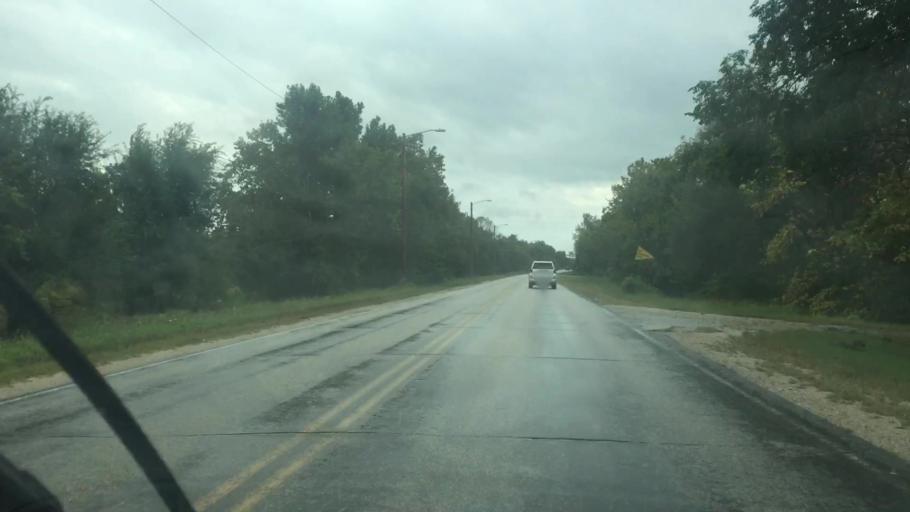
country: US
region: Kansas
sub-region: Allen County
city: Iola
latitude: 37.9139
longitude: -95.4091
